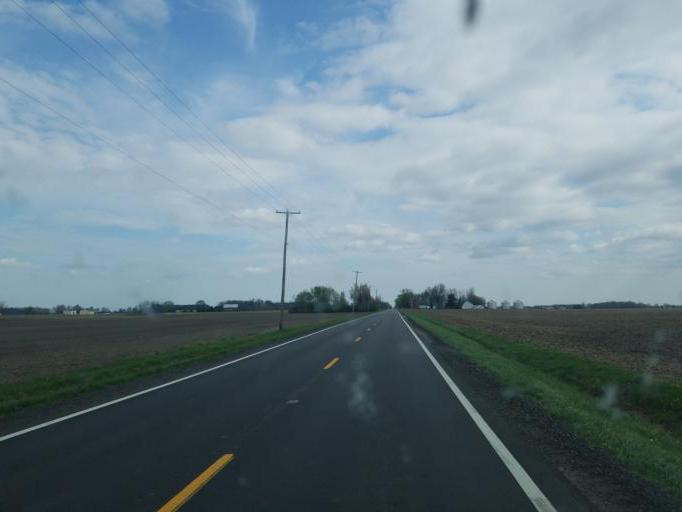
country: US
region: Ohio
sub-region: Marion County
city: Marion
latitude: 40.6229
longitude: -83.0278
